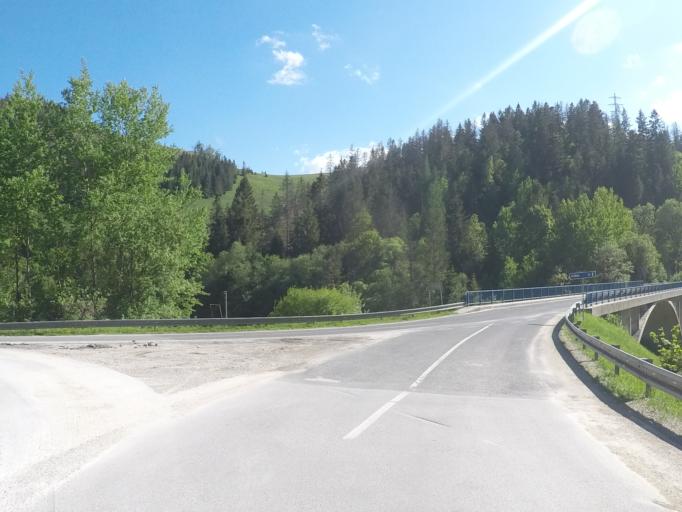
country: SK
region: Kosicky
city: Dobsina
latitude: 48.8540
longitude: 20.3858
